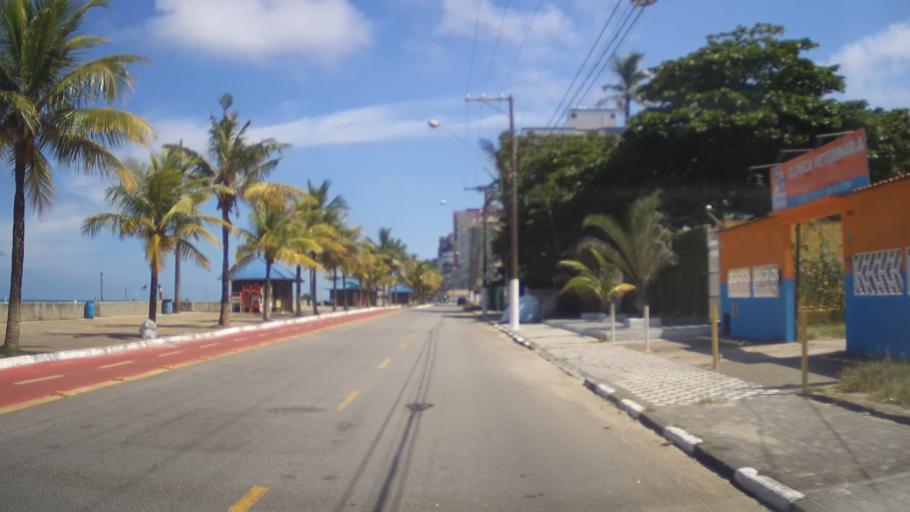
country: BR
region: Sao Paulo
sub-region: Mongagua
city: Mongagua
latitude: -24.0968
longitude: -46.6223
